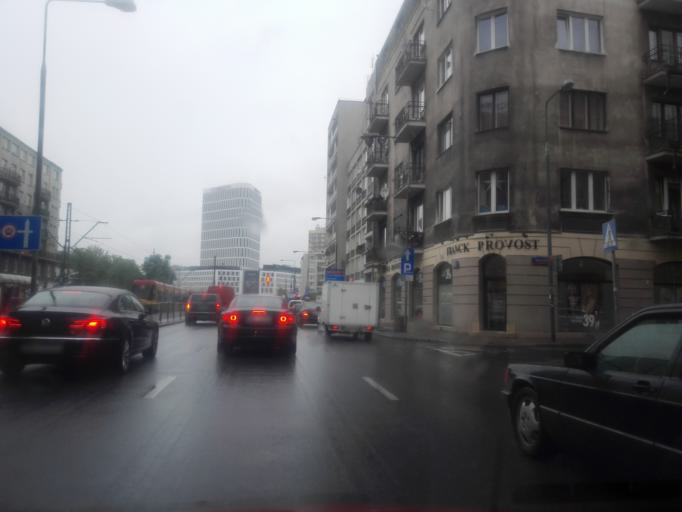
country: PL
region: Masovian Voivodeship
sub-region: Warszawa
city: Mokotow
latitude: 52.2088
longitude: 21.0217
